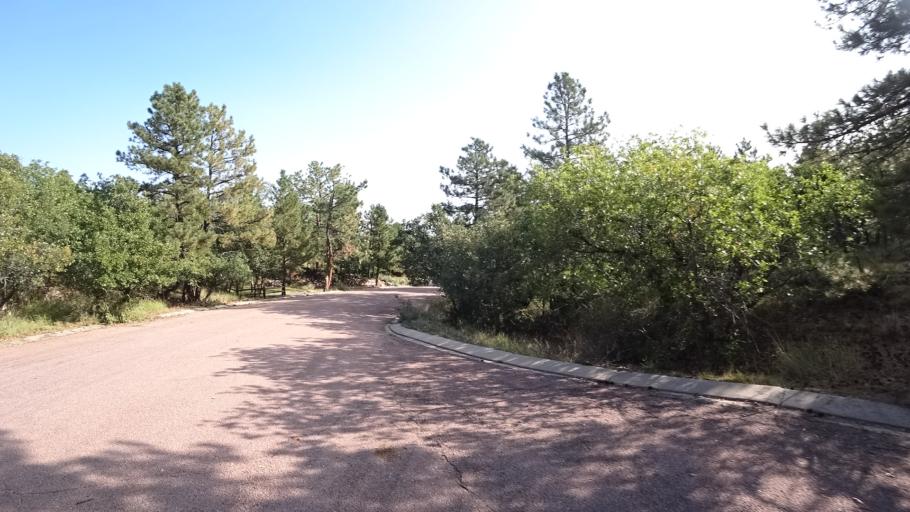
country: US
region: Colorado
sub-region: El Paso County
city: Colorado Springs
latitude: 38.8188
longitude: -104.8694
